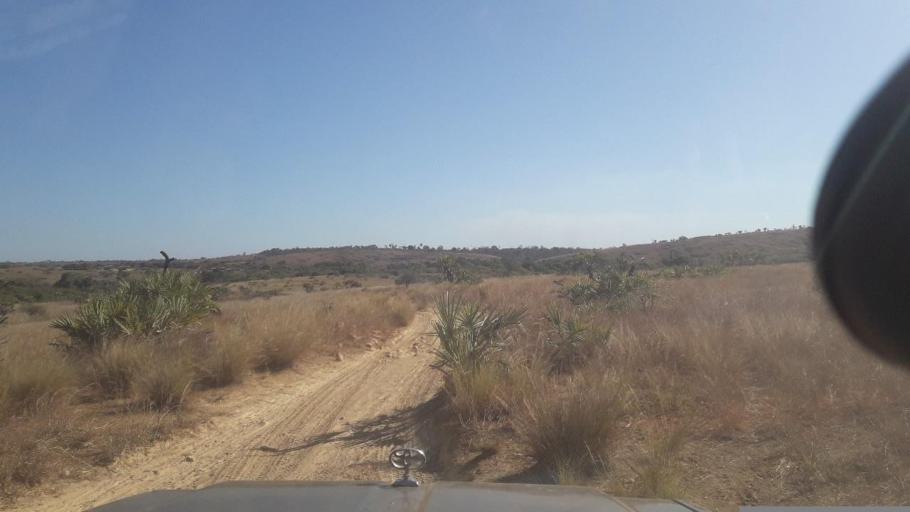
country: MG
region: Boeny
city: Sitampiky
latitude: -16.3742
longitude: 45.5936
